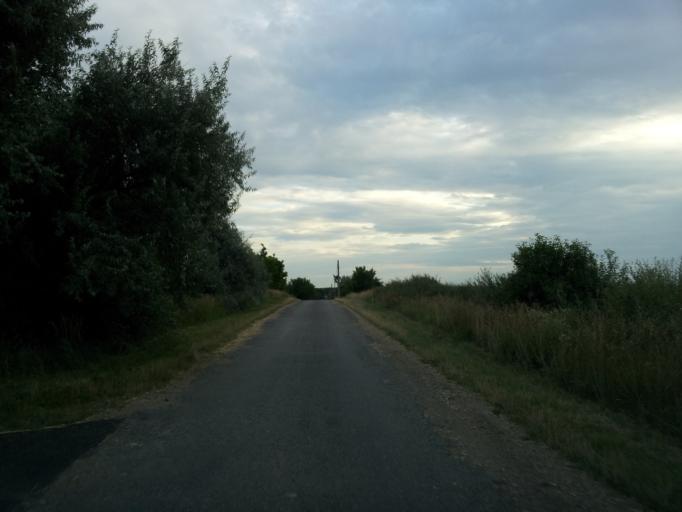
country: HU
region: Somogy
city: Balatonszabadi
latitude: 46.8882
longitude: 18.1632
